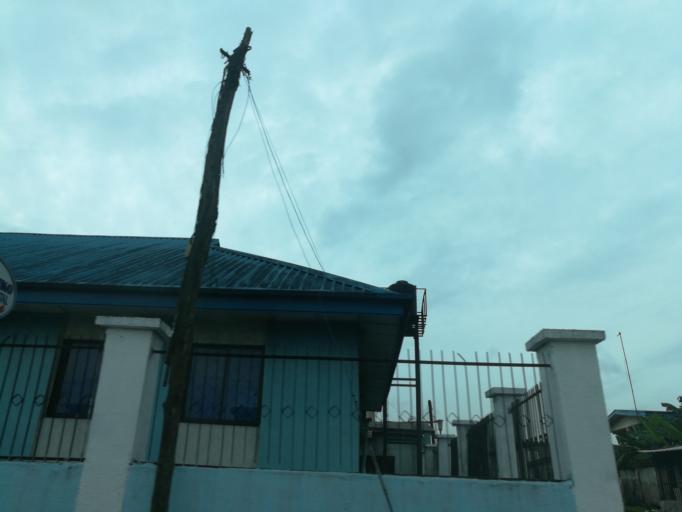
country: NG
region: Rivers
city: Port Harcourt
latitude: 4.8331
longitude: 7.0213
